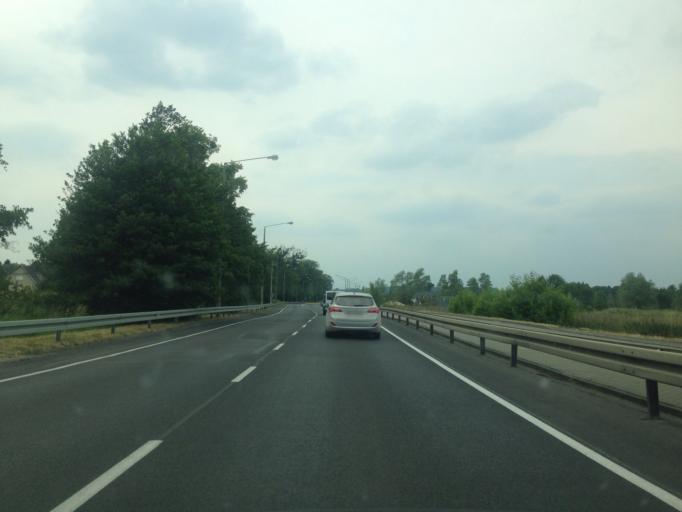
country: PL
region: Kujawsko-Pomorskie
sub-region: Grudziadz
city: Grudziadz
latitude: 53.5050
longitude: 18.8348
